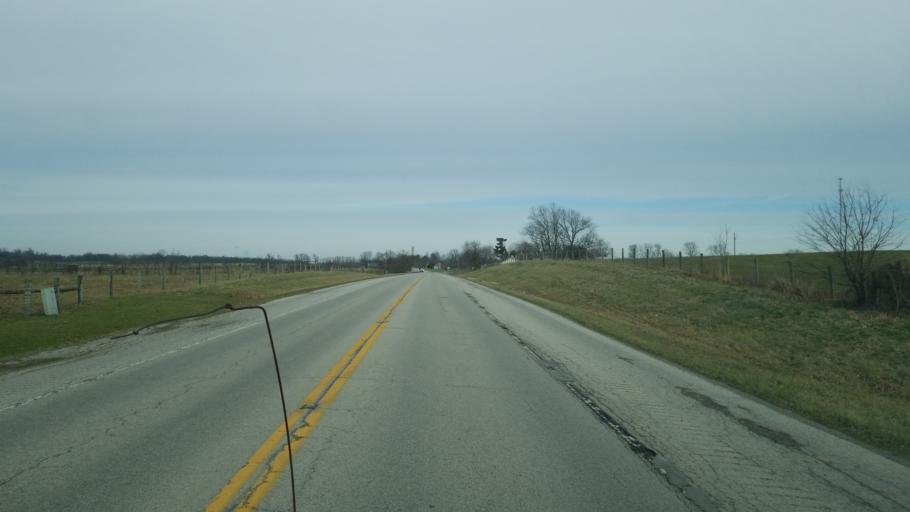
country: US
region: Kentucky
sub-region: Fleming County
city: Flemingsburg
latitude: 38.4925
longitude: -83.8559
